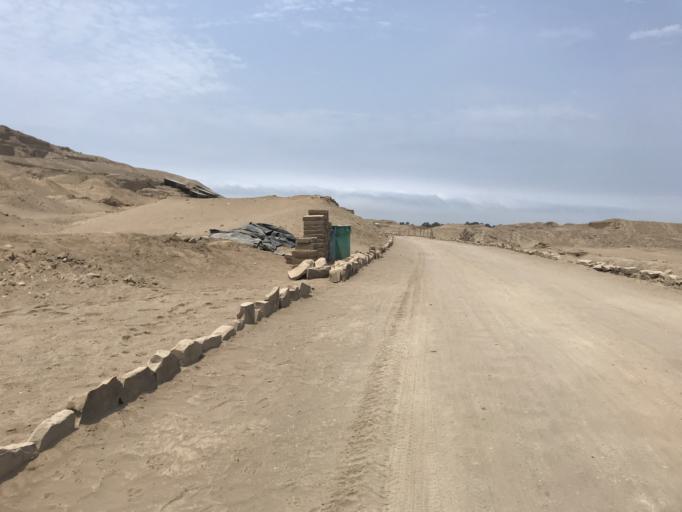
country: PE
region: Lima
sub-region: Lima
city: Punta Hermosa
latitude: -12.2588
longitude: -76.8995
